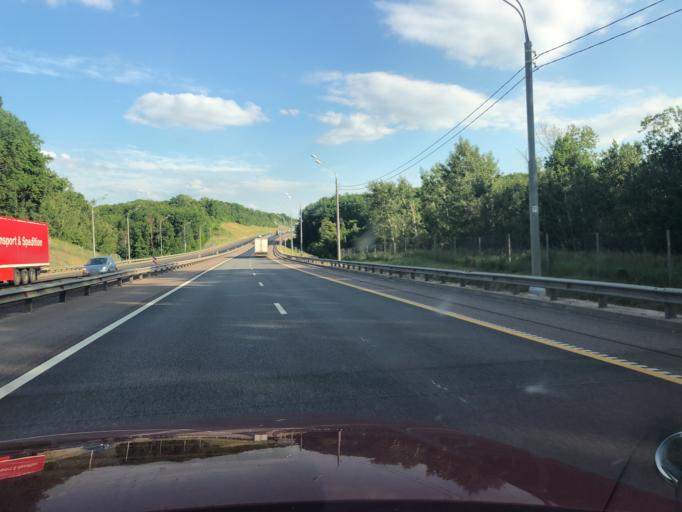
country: RU
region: Lipetsk
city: Zadonsk
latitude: 52.4061
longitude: 38.8546
